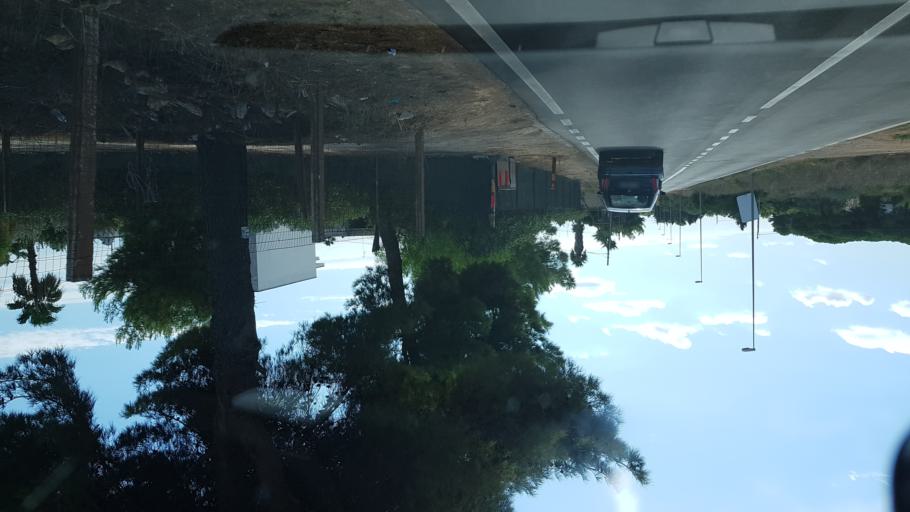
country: IT
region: Apulia
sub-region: Provincia di Lecce
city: Porto Cesareo
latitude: 40.2480
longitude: 17.9122
